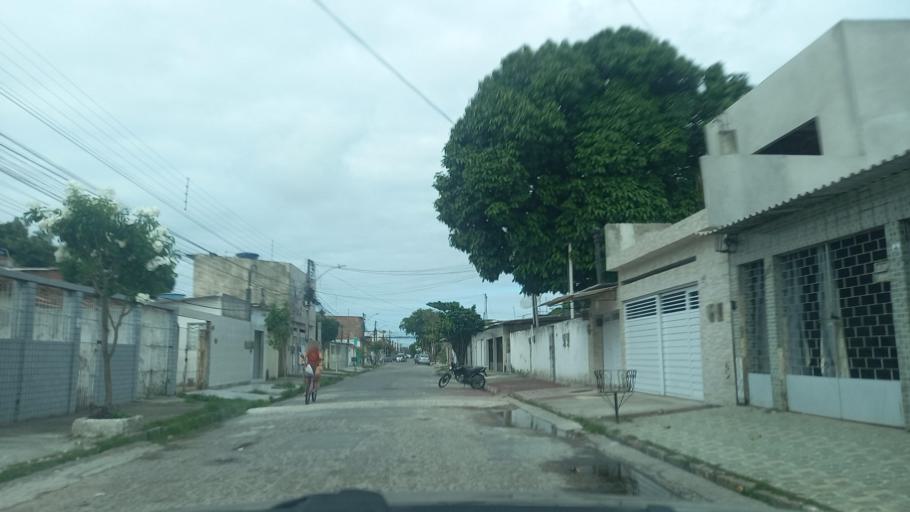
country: BR
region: Pernambuco
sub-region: Recife
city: Recife
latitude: -8.1089
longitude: -34.9206
